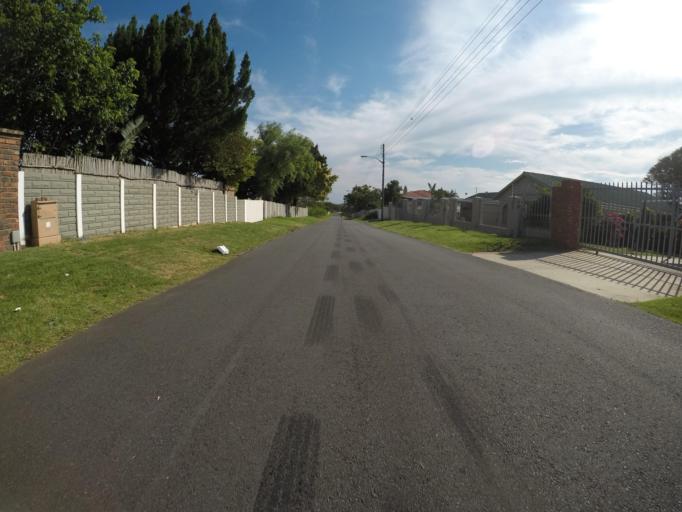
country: ZA
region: Eastern Cape
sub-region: Buffalo City Metropolitan Municipality
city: East London
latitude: -32.9442
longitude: 28.0046
